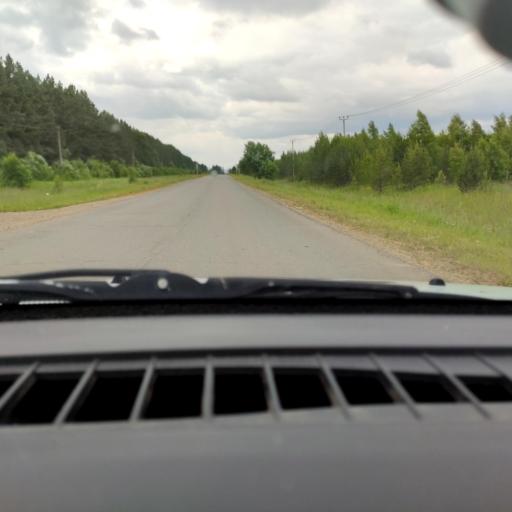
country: RU
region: Perm
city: Uinskoye
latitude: 57.1081
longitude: 56.6615
